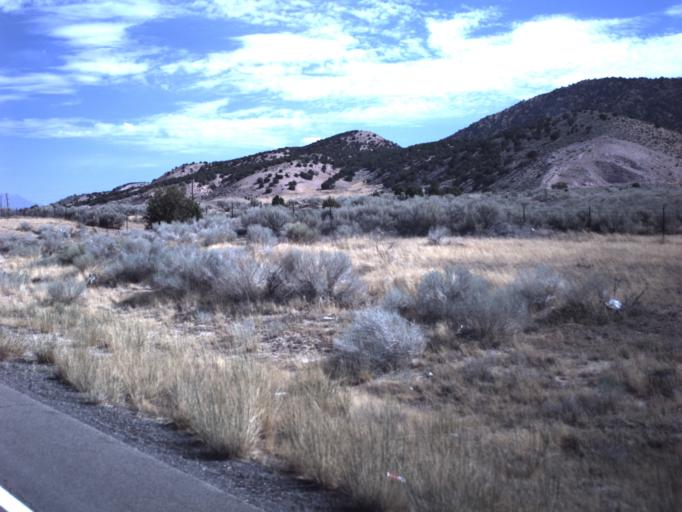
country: US
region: Utah
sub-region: Sanpete County
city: Gunnison
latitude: 39.4018
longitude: -111.9279
